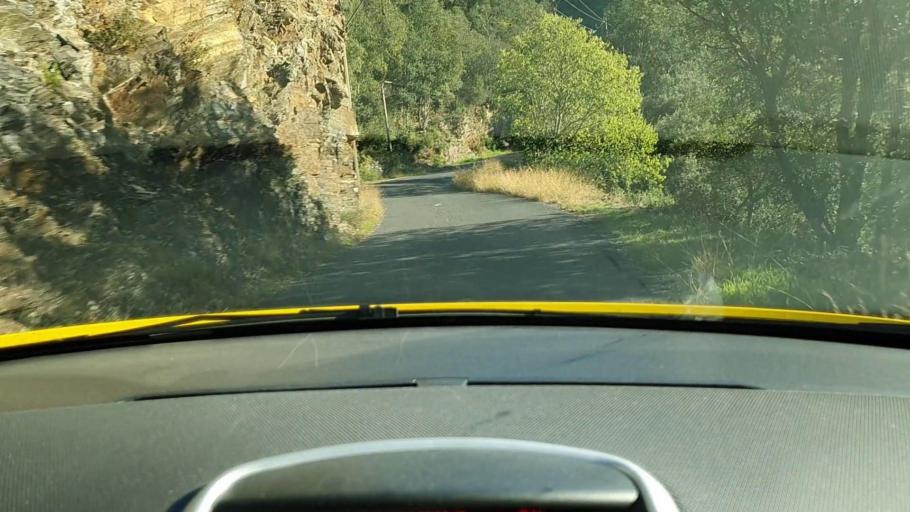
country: FR
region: Languedoc-Roussillon
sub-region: Departement du Gard
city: Sumene
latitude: 44.0199
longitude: 3.7346
